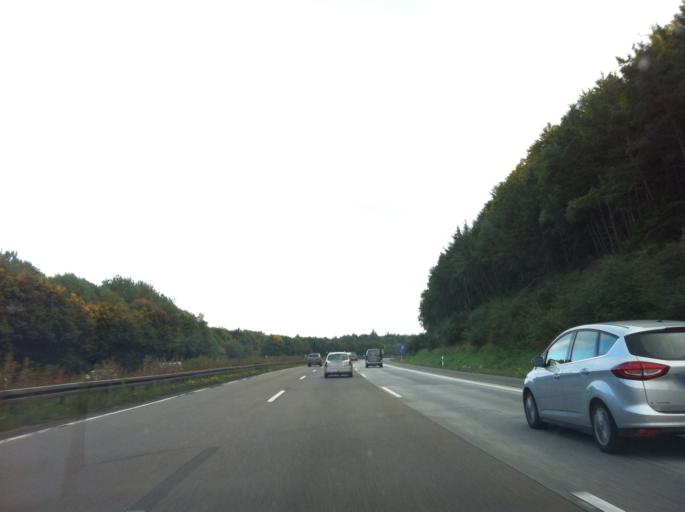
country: DE
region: Hesse
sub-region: Regierungsbezirk Darmstadt
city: Niedernhausen
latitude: 50.1750
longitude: 8.2801
